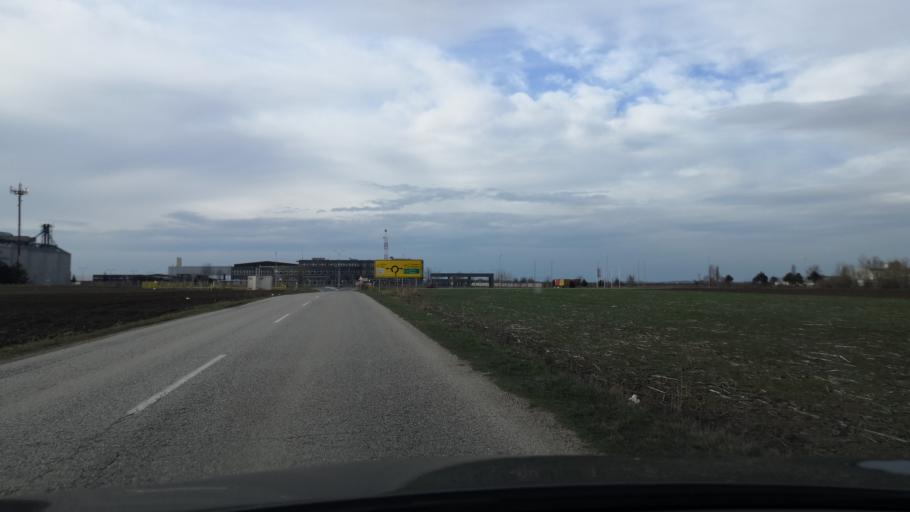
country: RS
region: Autonomna Pokrajina Vojvodina
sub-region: Sremski Okrug
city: Ingija
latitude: 45.0535
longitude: 20.1046
